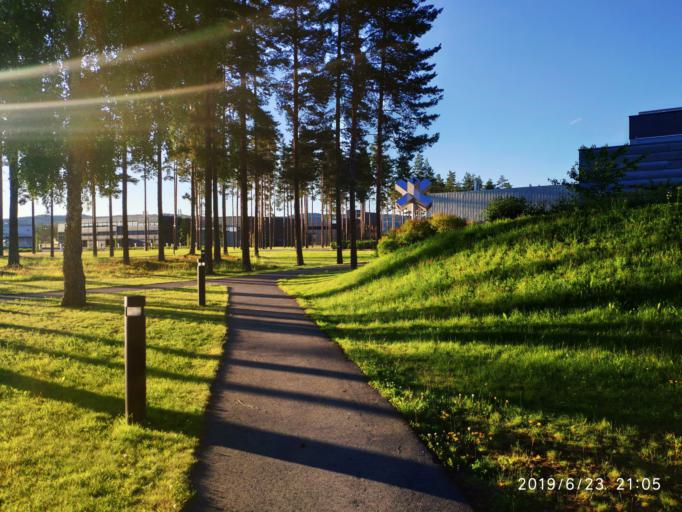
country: NO
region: Buskerud
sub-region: Ringerike
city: Honefoss
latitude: 60.2084
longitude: 10.3184
